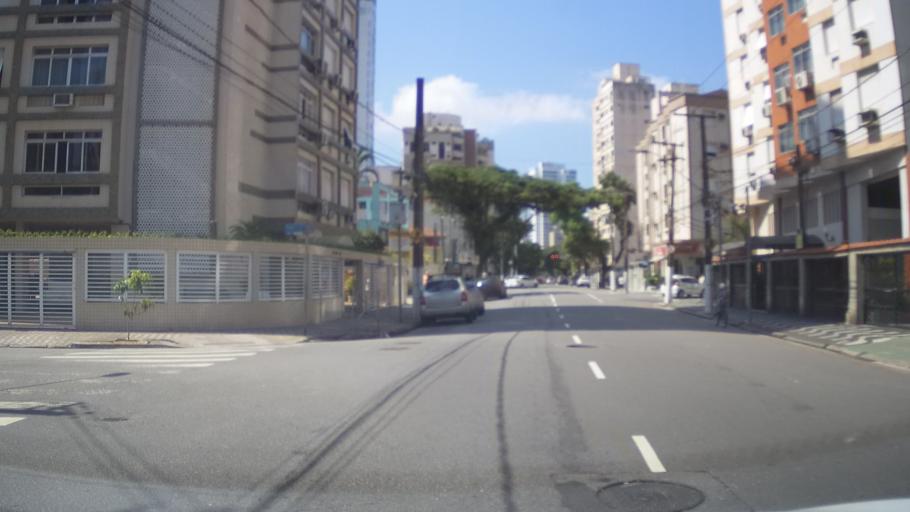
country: BR
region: Sao Paulo
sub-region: Santos
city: Santos
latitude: -23.9803
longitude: -46.3089
